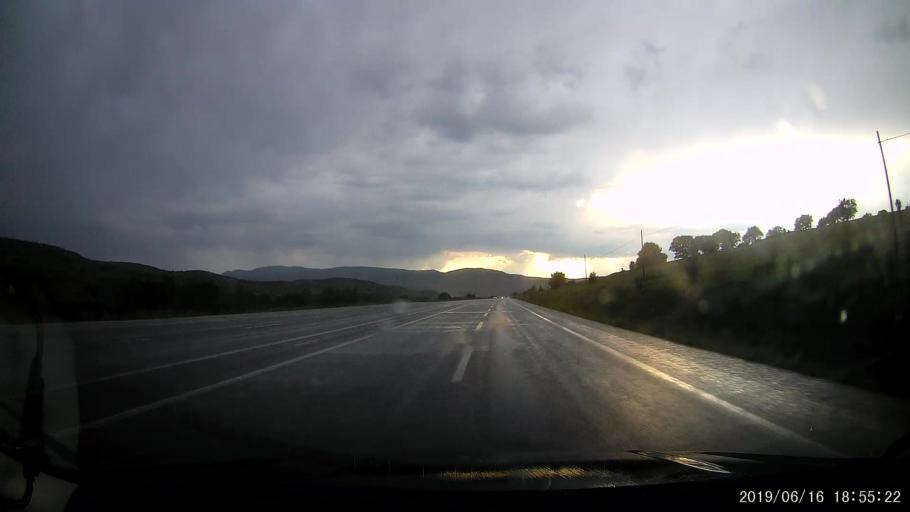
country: TR
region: Erzincan
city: Refahiye
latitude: 39.8997
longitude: 38.8297
